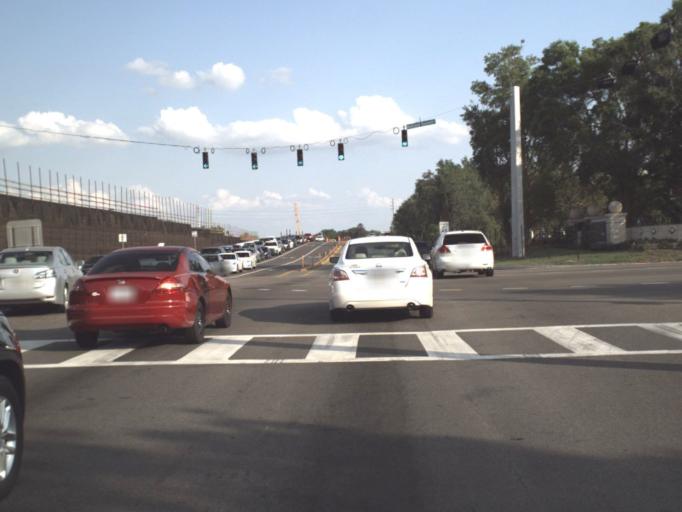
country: US
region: Florida
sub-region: Orange County
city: Eatonville
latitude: 28.6361
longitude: -81.4032
